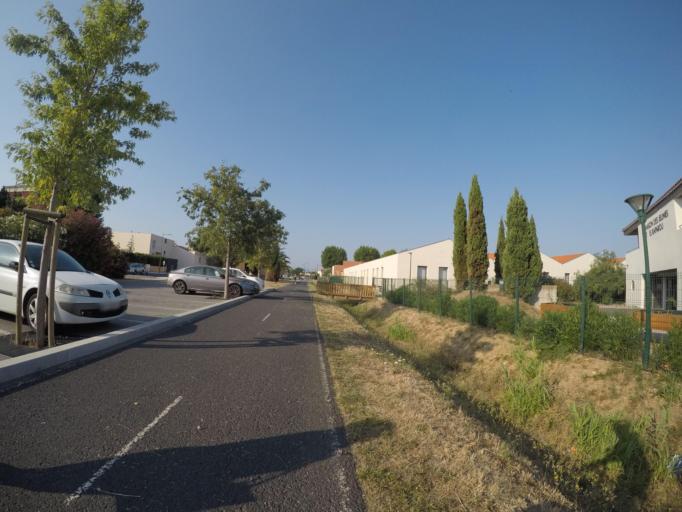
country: FR
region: Languedoc-Roussillon
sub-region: Departement des Pyrenees-Orientales
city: Canohes
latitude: 42.6533
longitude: 2.8316
